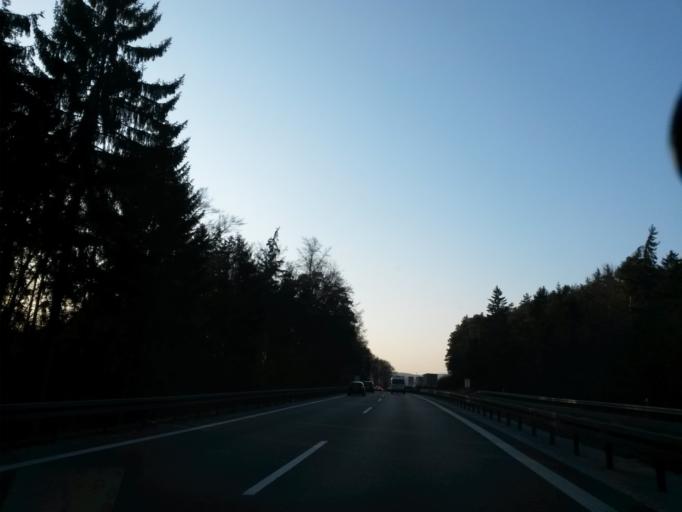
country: DE
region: Bavaria
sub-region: Upper Bavaria
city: Denkendorf
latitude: 48.9768
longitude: 11.4008
